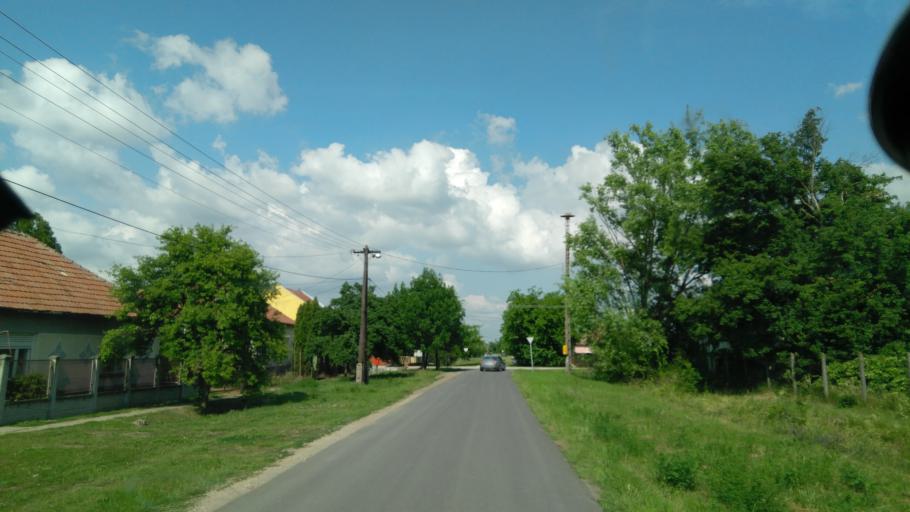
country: HU
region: Bekes
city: Doboz
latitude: 46.7389
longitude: 21.2352
